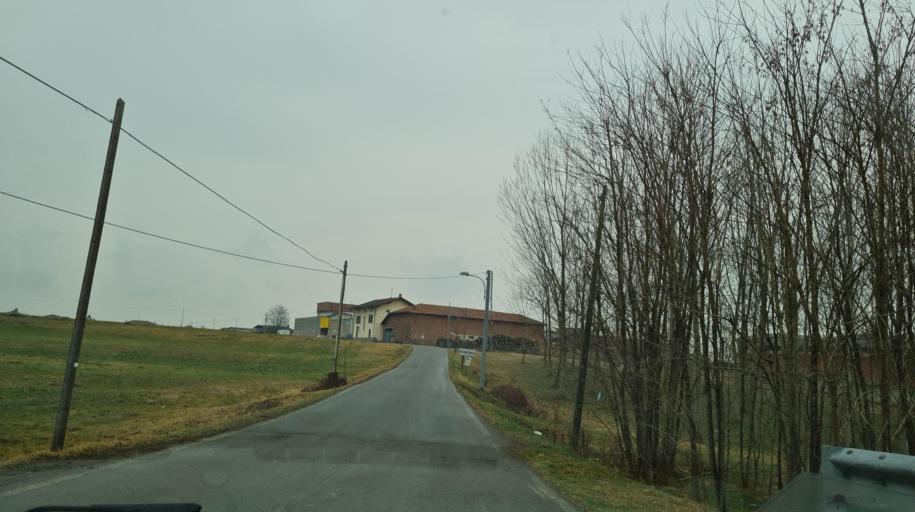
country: IT
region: Piedmont
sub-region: Provincia di Biella
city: Borriana
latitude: 45.5106
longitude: 8.0330
